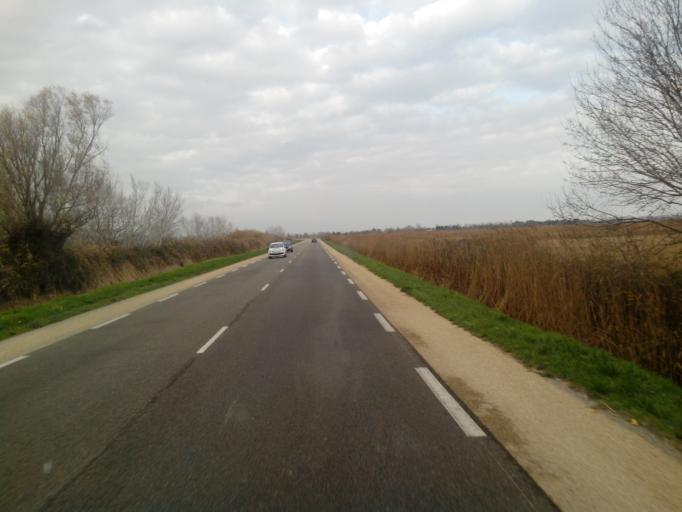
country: FR
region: Provence-Alpes-Cote d'Azur
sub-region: Departement des Bouches-du-Rhone
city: Saintes-Maries-de-la-Mer
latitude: 43.5631
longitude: 4.4197
